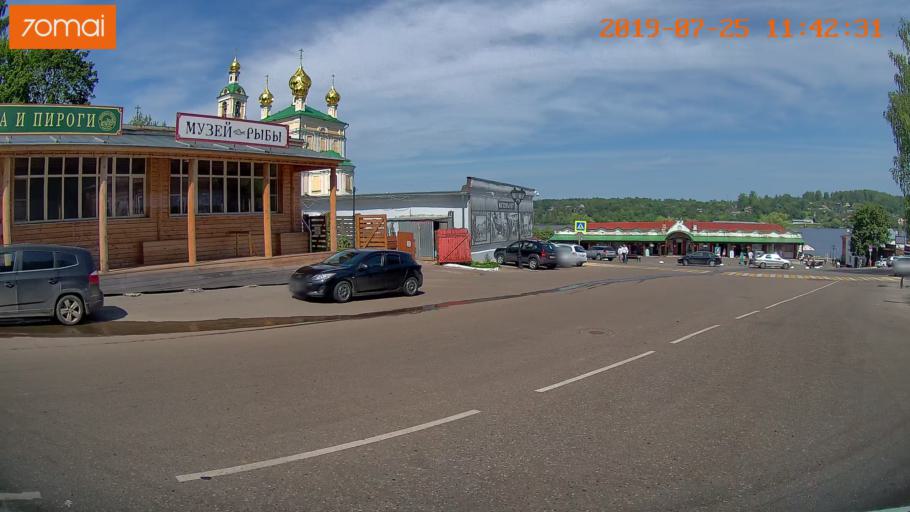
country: RU
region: Ivanovo
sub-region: Privolzhskiy Rayon
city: Ples
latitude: 57.4600
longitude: 41.5121
